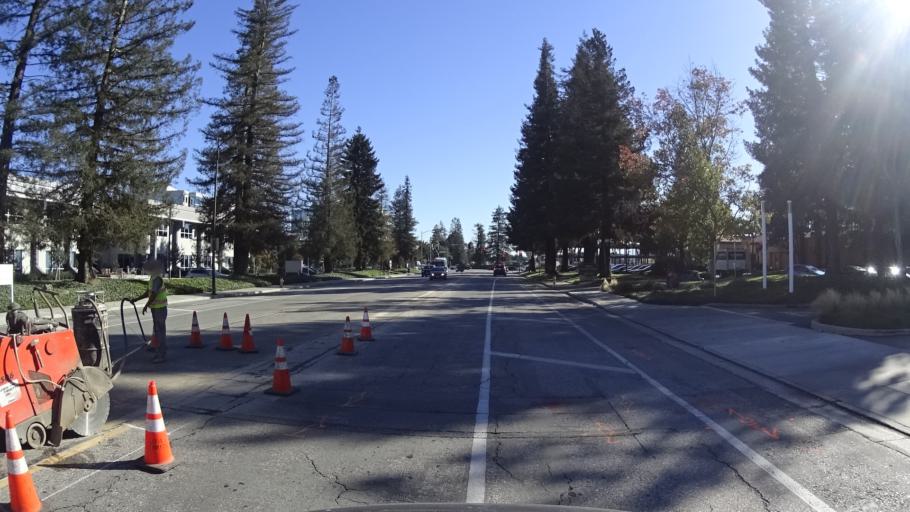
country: US
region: California
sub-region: Santa Clara County
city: San Jose
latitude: 37.3665
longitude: -121.9180
